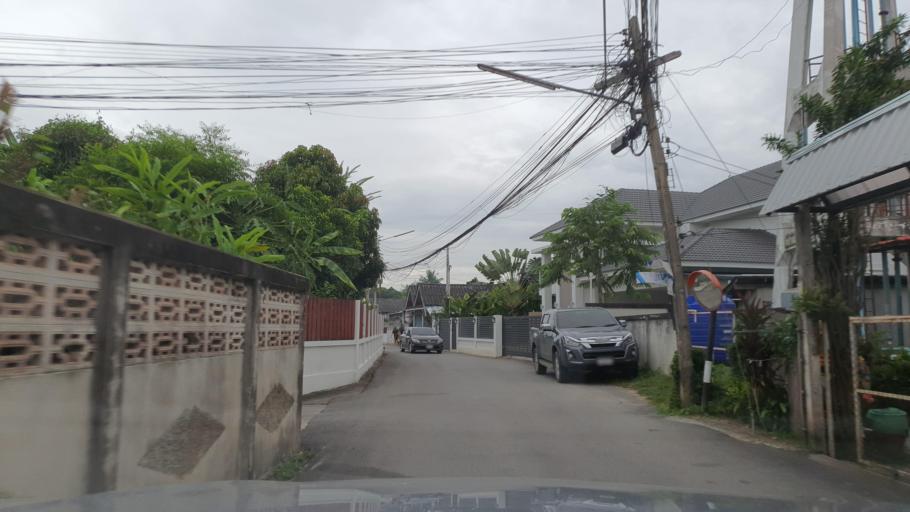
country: TH
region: Chiang Mai
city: San Sai
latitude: 18.9221
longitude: 98.9436
